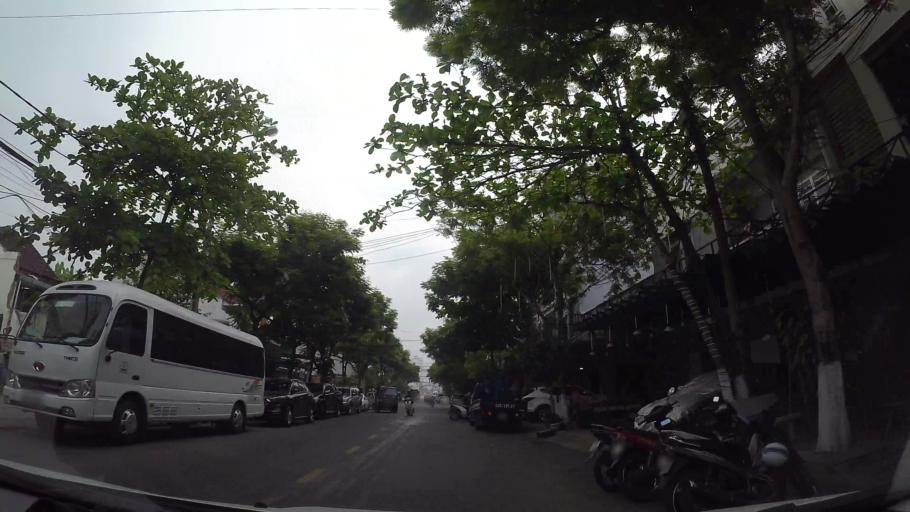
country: VN
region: Da Nang
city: Son Tra
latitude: 16.0499
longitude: 108.2400
